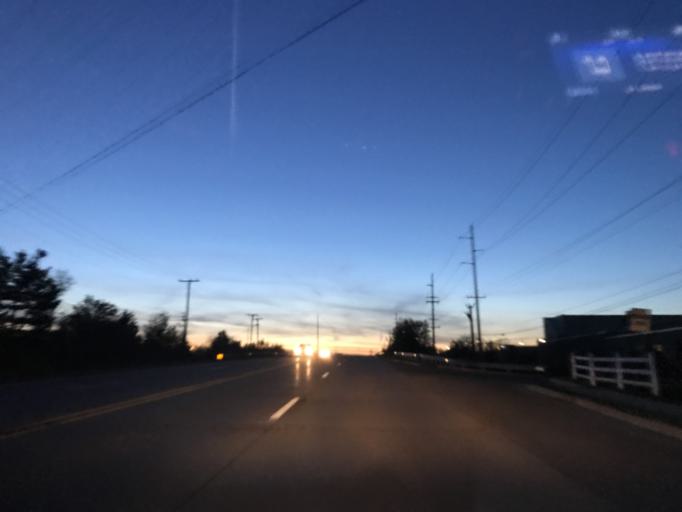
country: US
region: Michigan
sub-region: Oakland County
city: Novi
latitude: 42.4683
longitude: -83.4288
